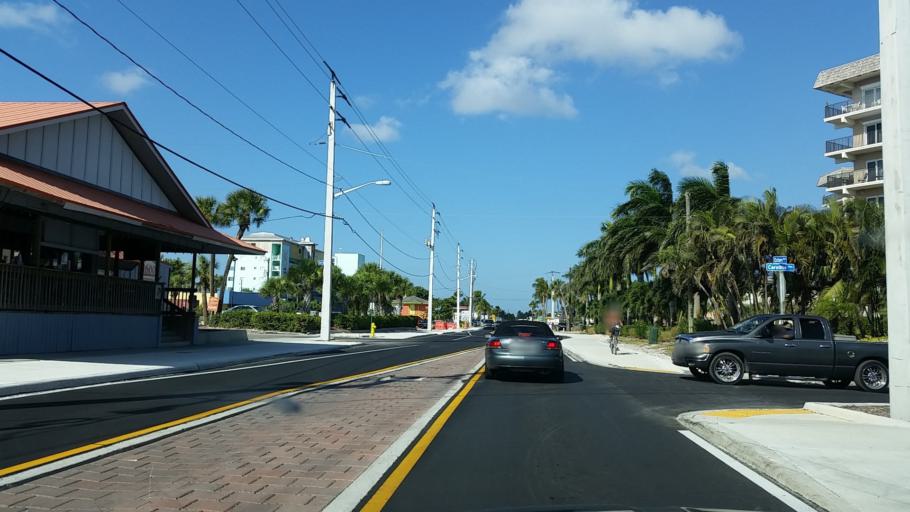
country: US
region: Florida
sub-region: Lee County
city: Fort Myers Beach
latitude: 26.4511
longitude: -81.9494
